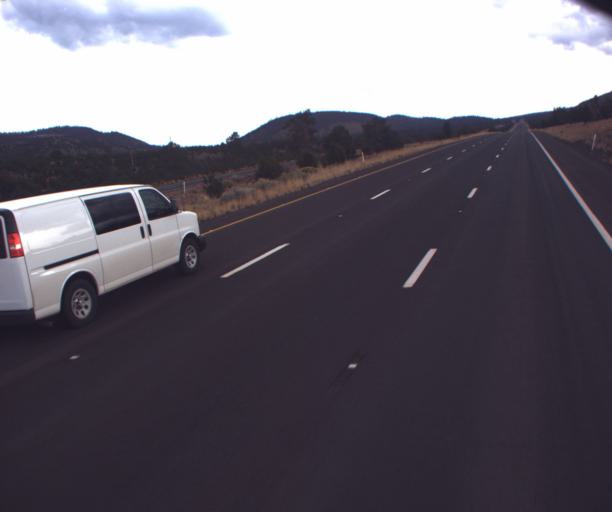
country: US
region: Arizona
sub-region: Coconino County
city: Flagstaff
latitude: 35.4191
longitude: -111.5715
